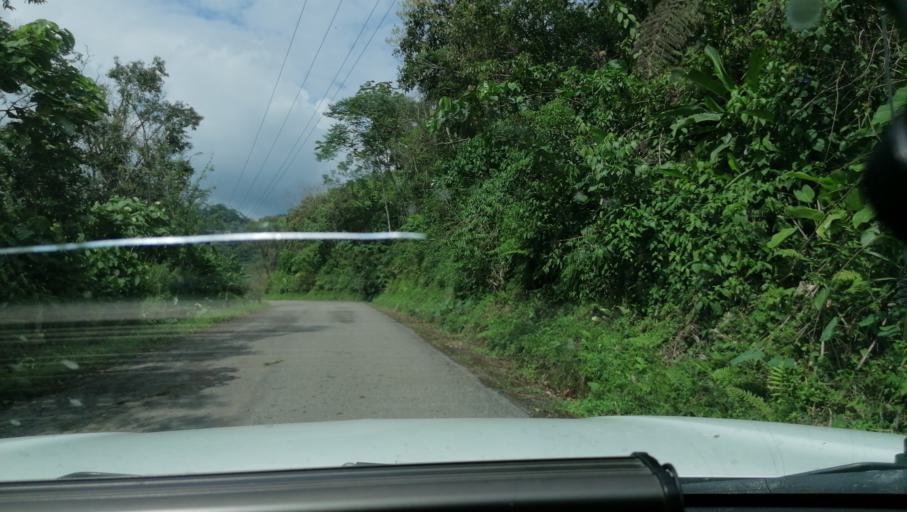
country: MX
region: Chiapas
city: Ocotepec
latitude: 17.3207
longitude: -93.1687
